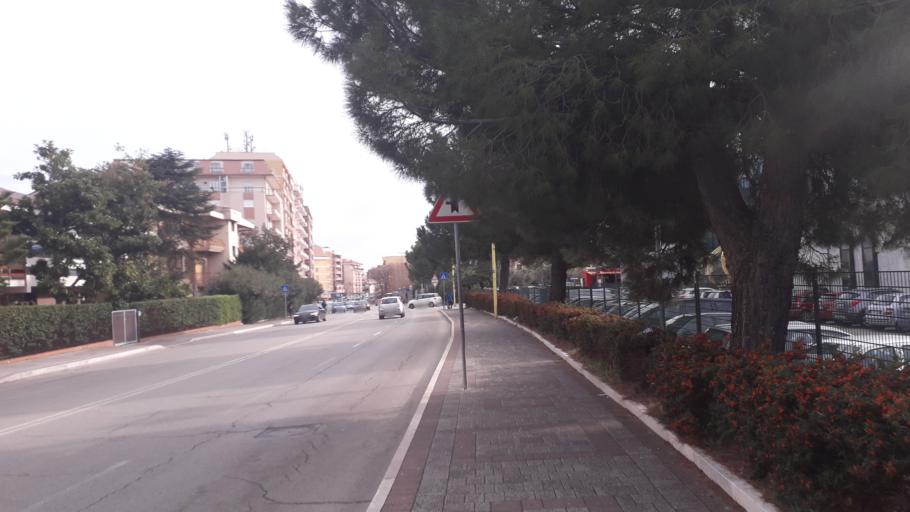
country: IT
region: Molise
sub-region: Provincia di Campobasso
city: Termoli
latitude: 41.9992
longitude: 14.9870
